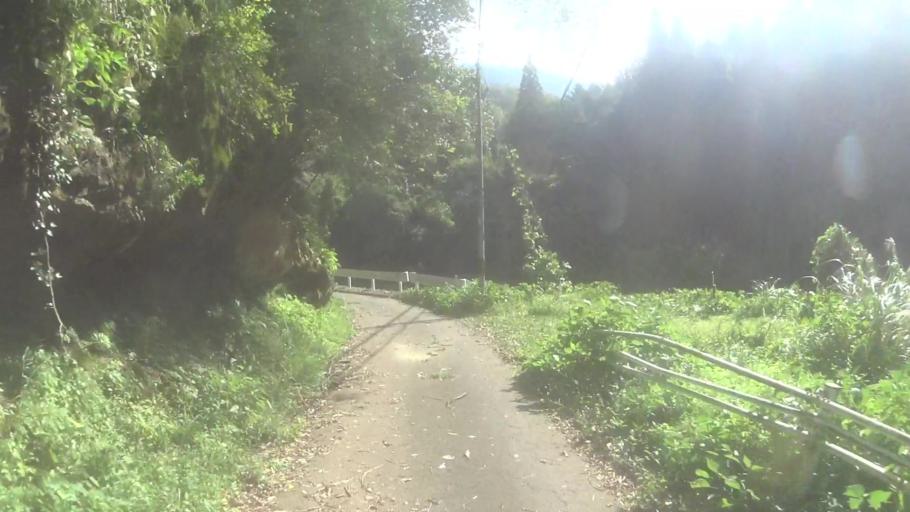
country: JP
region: Kyoto
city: Miyazu
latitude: 35.7205
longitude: 135.1638
